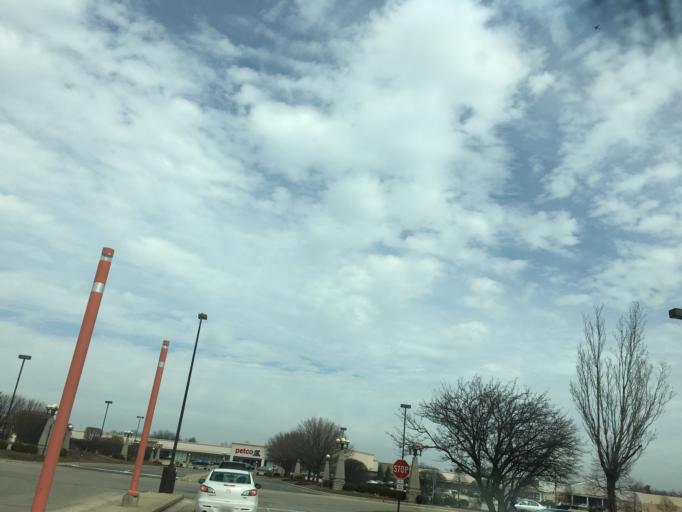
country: US
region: Illinois
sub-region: DuPage County
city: Woodridge
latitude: 41.7518
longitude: -88.0176
